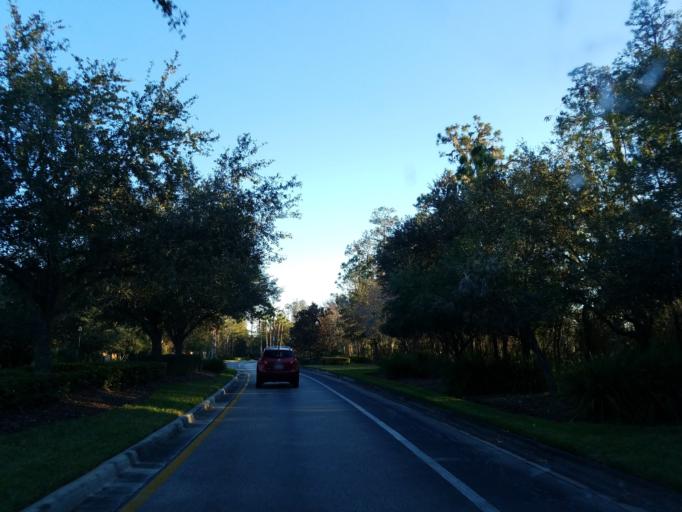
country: US
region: Florida
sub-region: Pasco County
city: Wesley Chapel
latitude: 28.2023
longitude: -82.3660
